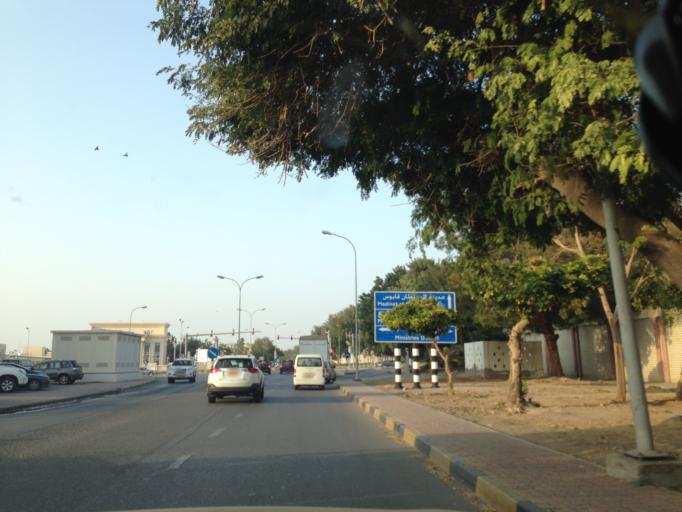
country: OM
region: Muhafazat Masqat
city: Bawshar
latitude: 23.5962
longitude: 58.4494
